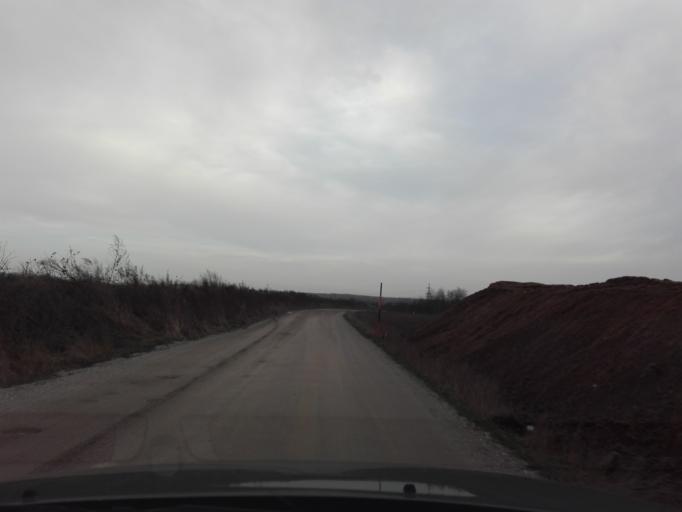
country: AT
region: Upper Austria
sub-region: Politischer Bezirk Linz-Land
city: Horsching
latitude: 48.2171
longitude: 14.1545
